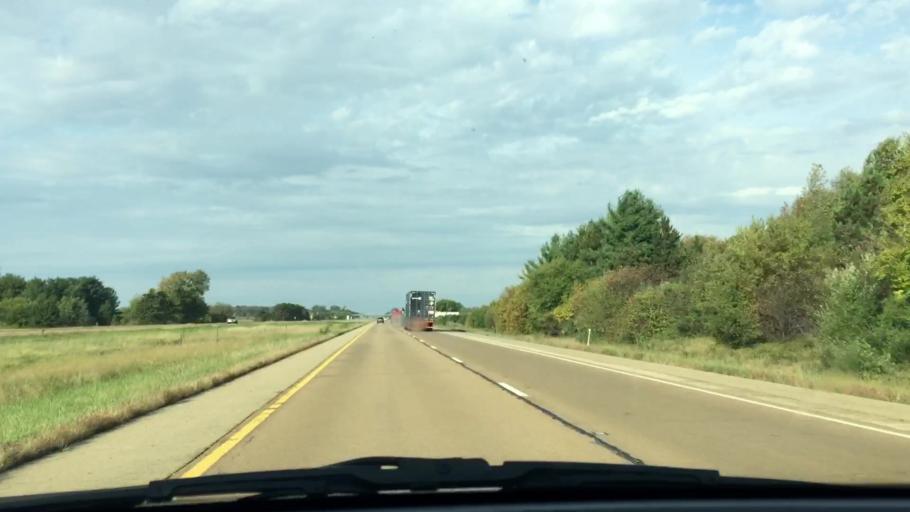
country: US
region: Illinois
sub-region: Whiteside County
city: Rock Falls
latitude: 41.7516
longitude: -89.6682
